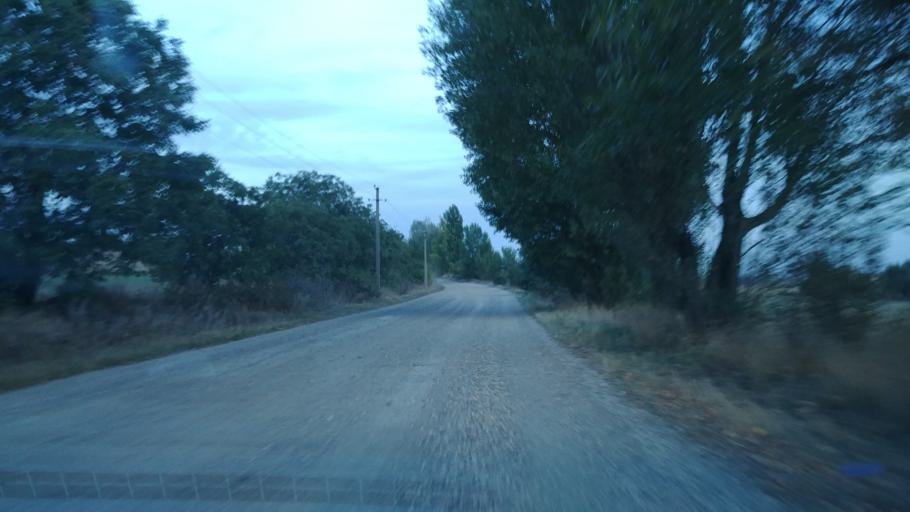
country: MD
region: Rezina
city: Saharna
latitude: 47.6772
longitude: 28.9258
